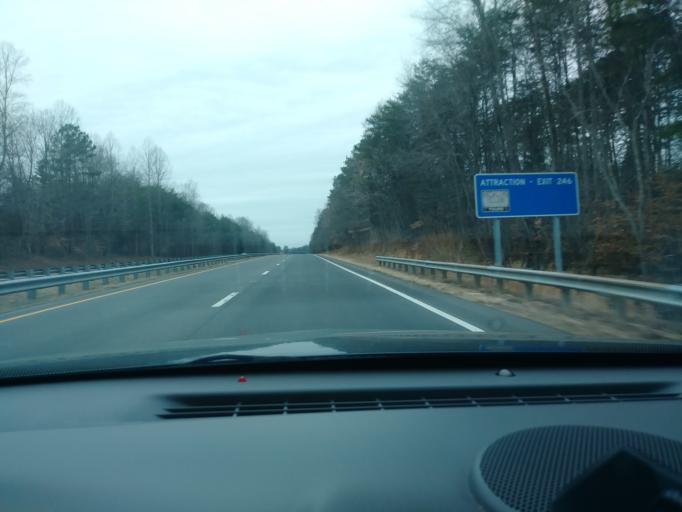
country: US
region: North Carolina
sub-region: Forsyth County
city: Lewisville
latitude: 36.0976
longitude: -80.4566
